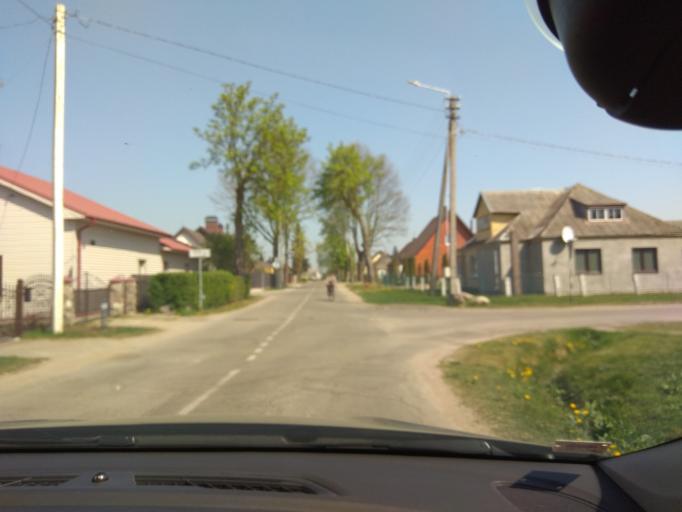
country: LT
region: Siauliu apskritis
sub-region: Joniskis
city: Joniskis
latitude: 56.2473
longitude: 23.6153
